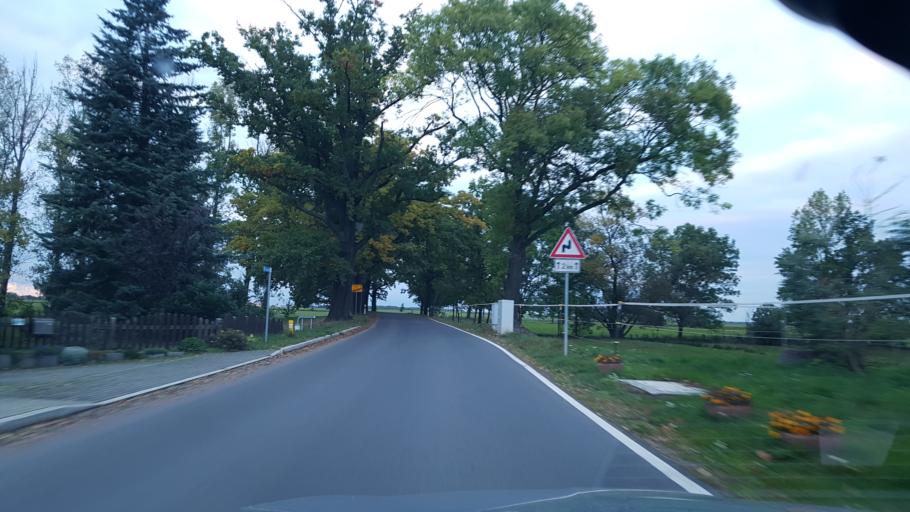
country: DE
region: Saxony
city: Grossenhain
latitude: 51.3207
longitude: 13.5809
